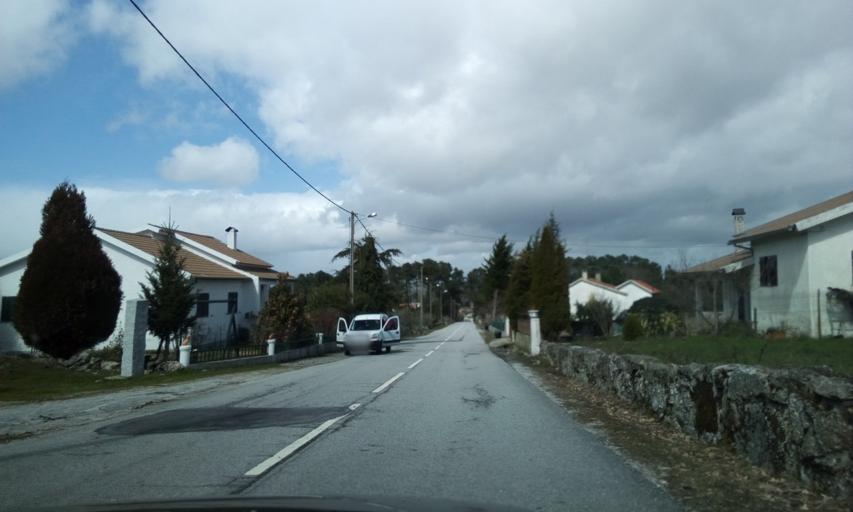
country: PT
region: Guarda
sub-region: Fornos de Algodres
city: Fornos de Algodres
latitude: 40.6403
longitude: -7.5489
